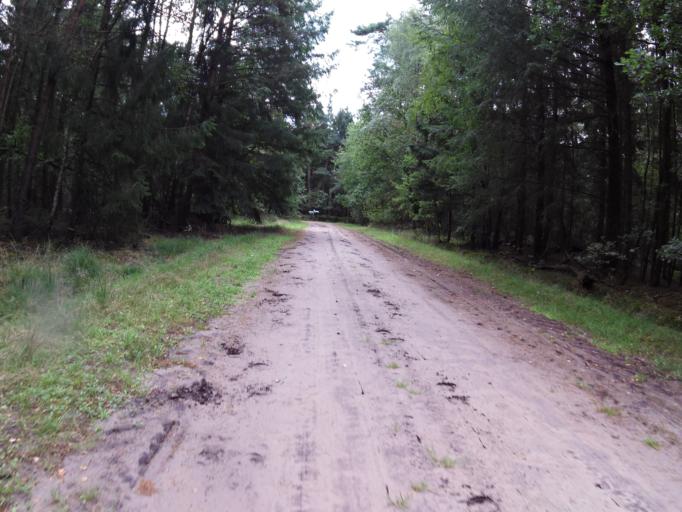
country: DE
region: Lower Saxony
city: Sandbostel
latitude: 53.3689
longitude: 9.1533
